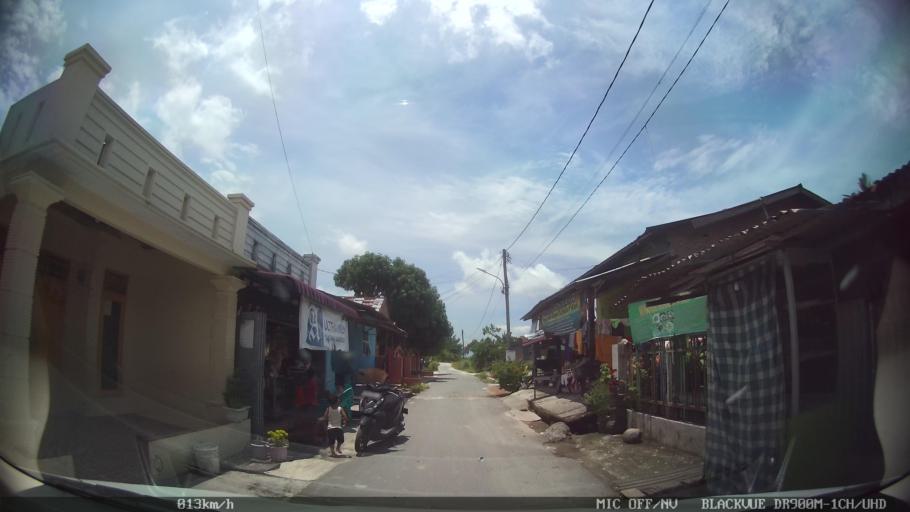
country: ID
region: North Sumatra
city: Percut
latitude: 3.5507
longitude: 98.8514
